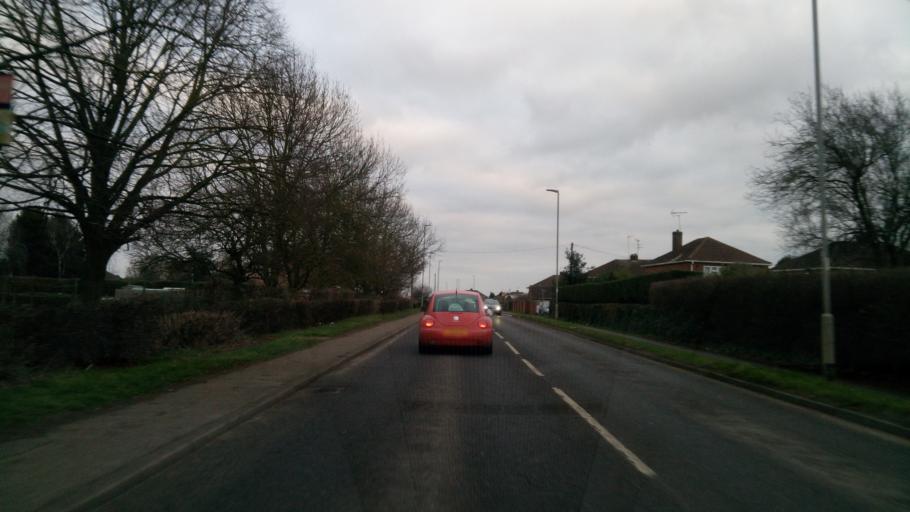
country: GB
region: England
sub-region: Peterborough
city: Peterborough
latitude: 52.5512
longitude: -0.2222
